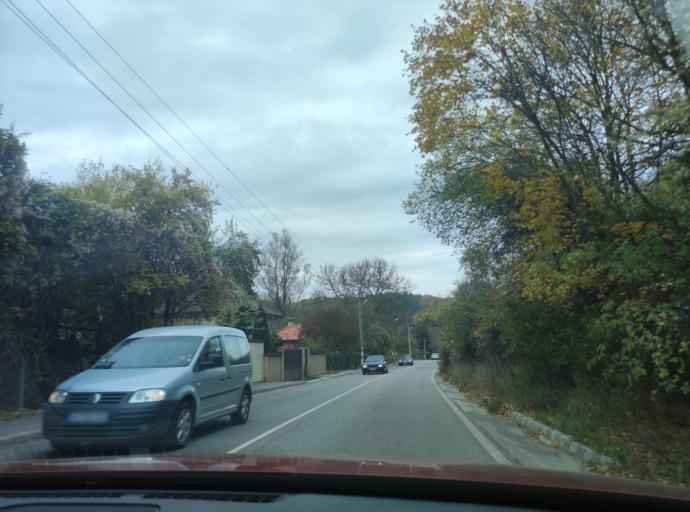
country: BG
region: Sofiya
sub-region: Obshtina Godech
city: Godech
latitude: 42.9709
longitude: 23.1420
